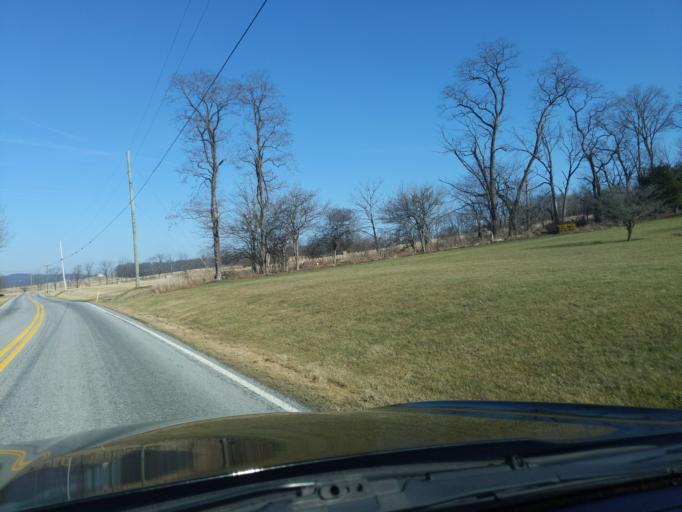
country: US
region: Pennsylvania
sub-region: Blair County
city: Tipton
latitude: 40.5982
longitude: -78.2661
